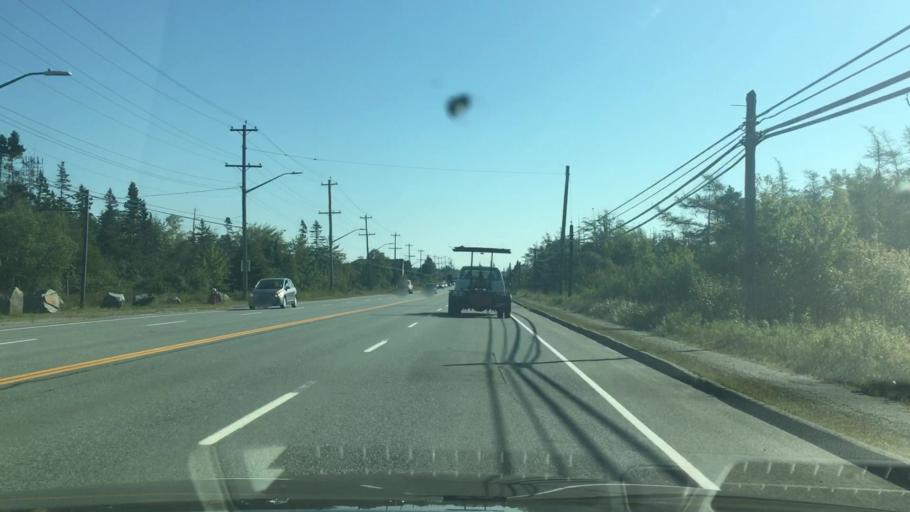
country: CA
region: Nova Scotia
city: Cole Harbour
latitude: 44.7017
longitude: -63.4770
